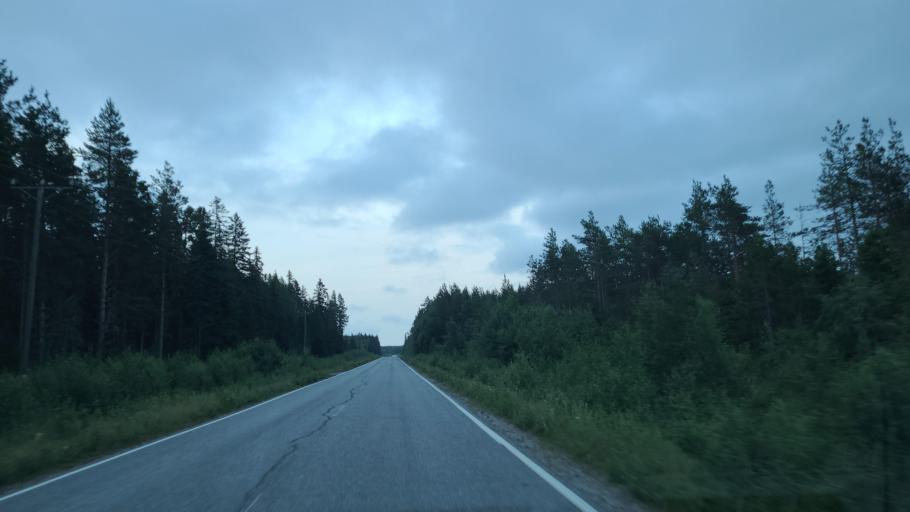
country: FI
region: Ostrobothnia
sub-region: Vaasa
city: Replot
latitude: 63.2278
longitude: 21.2238
